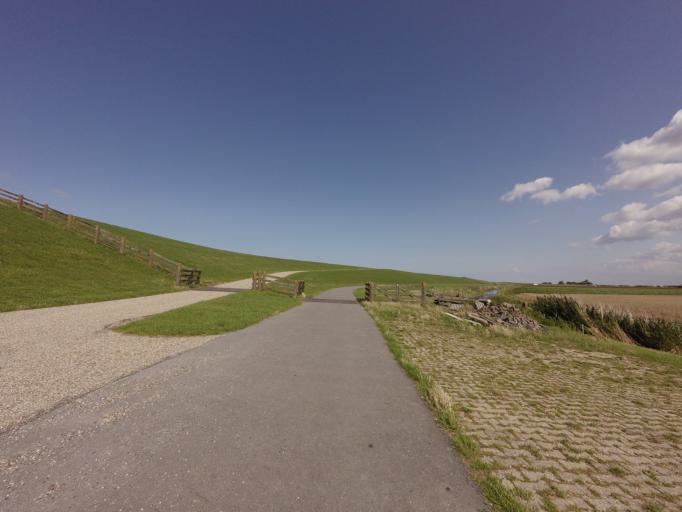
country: NL
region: Friesland
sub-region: Gemeente Dongeradeel
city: Holwerd
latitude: 53.3763
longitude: 5.8784
